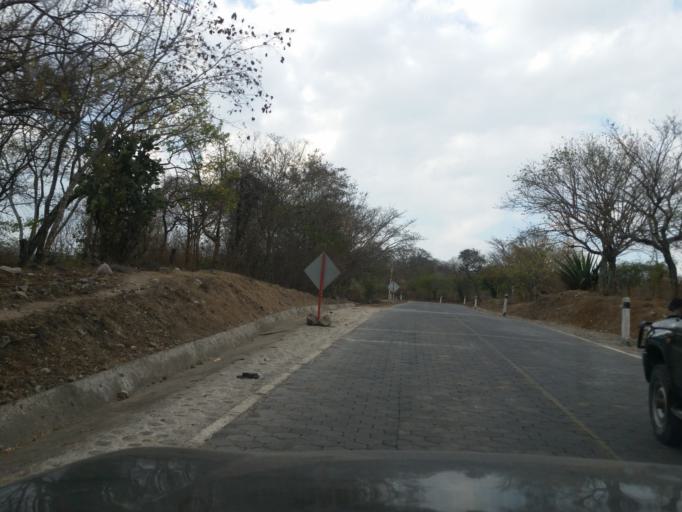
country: NI
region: Jinotega
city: La Concordia
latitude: 13.1759
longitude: -86.1680
